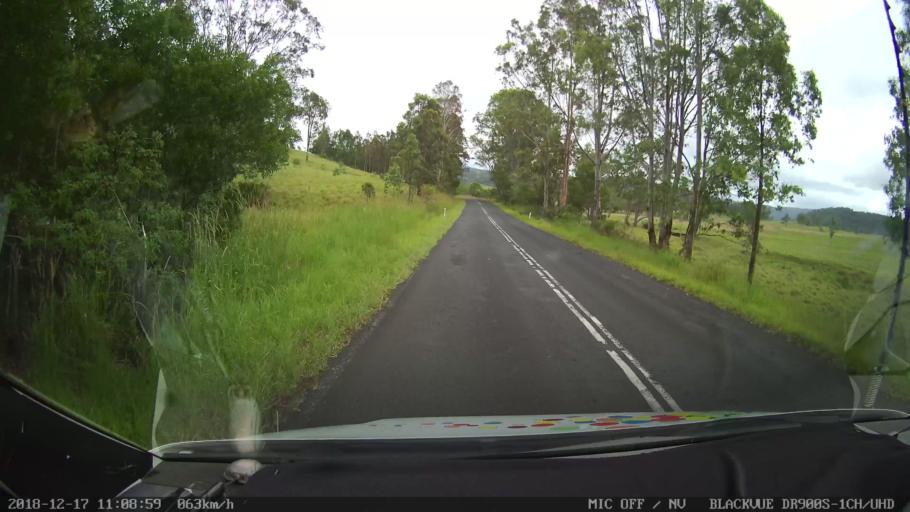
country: AU
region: New South Wales
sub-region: Kyogle
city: Kyogle
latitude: -28.7583
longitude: 152.6555
